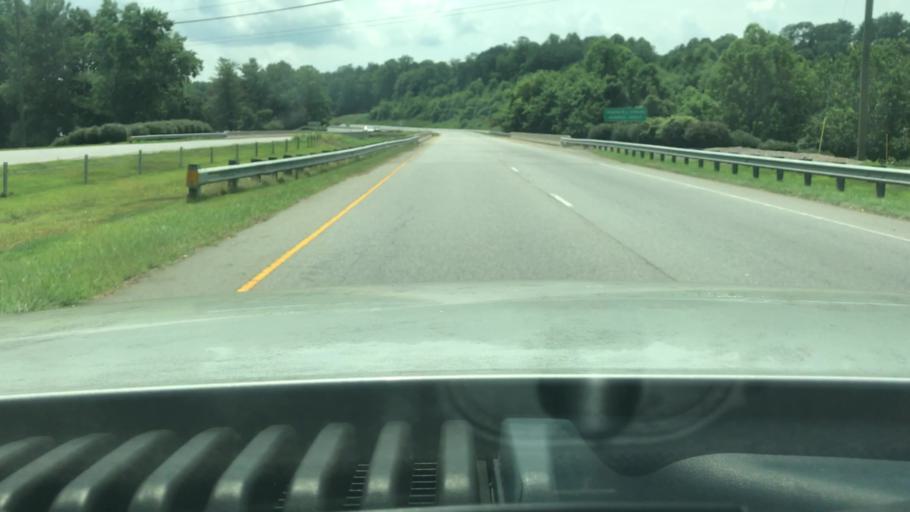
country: US
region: North Carolina
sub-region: Wilkes County
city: Wilkesboro
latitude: 36.1420
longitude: -81.1745
